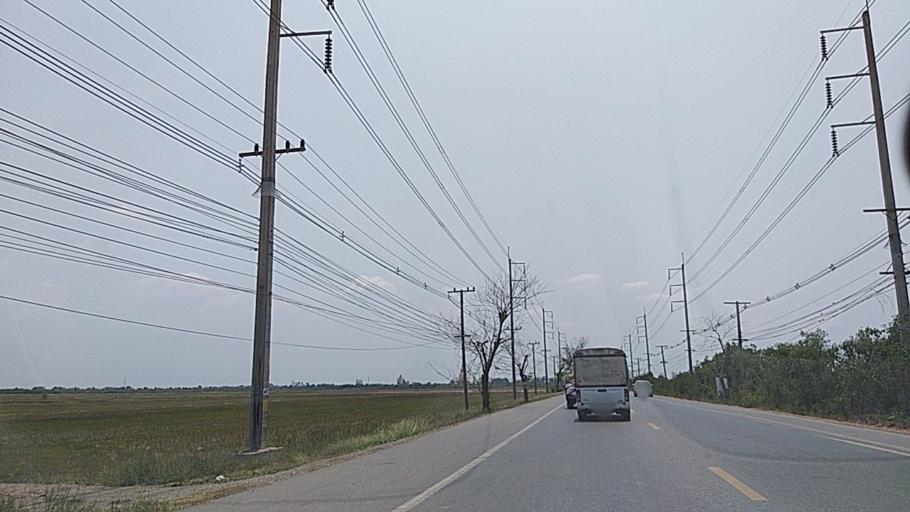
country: TH
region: Chachoengsao
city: Bang Nam Priao
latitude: 13.8168
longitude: 101.0535
